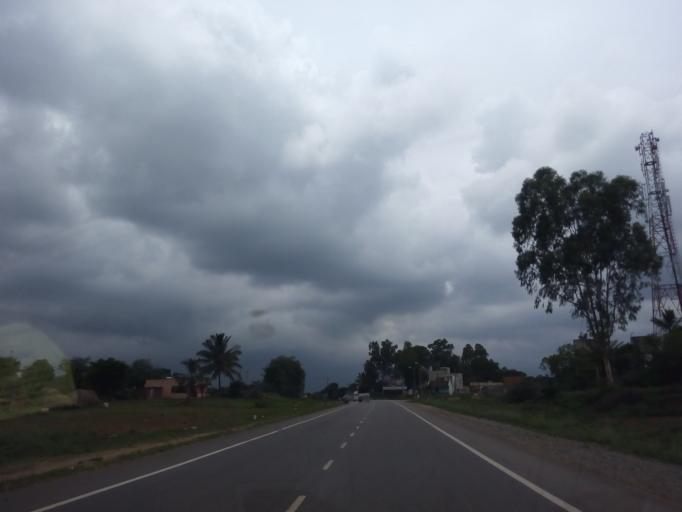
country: IN
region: Karnataka
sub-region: Hassan
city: Hassan
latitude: 12.9989
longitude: 76.1267
